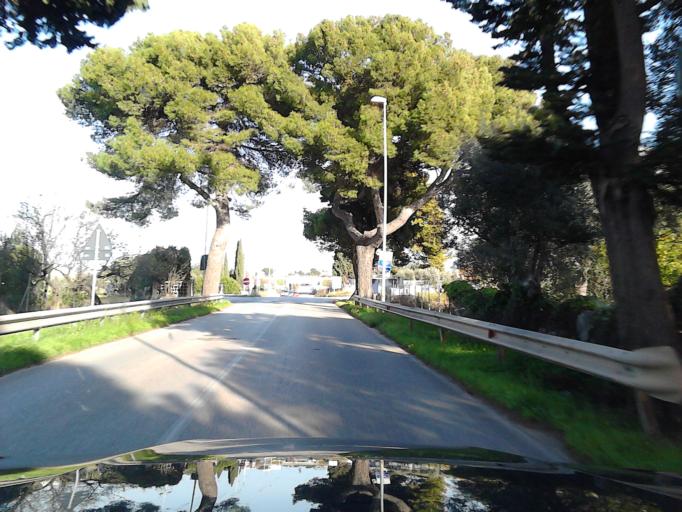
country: IT
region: Apulia
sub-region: Provincia di Bari
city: Mola di Bari
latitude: 41.0490
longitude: 17.0710
